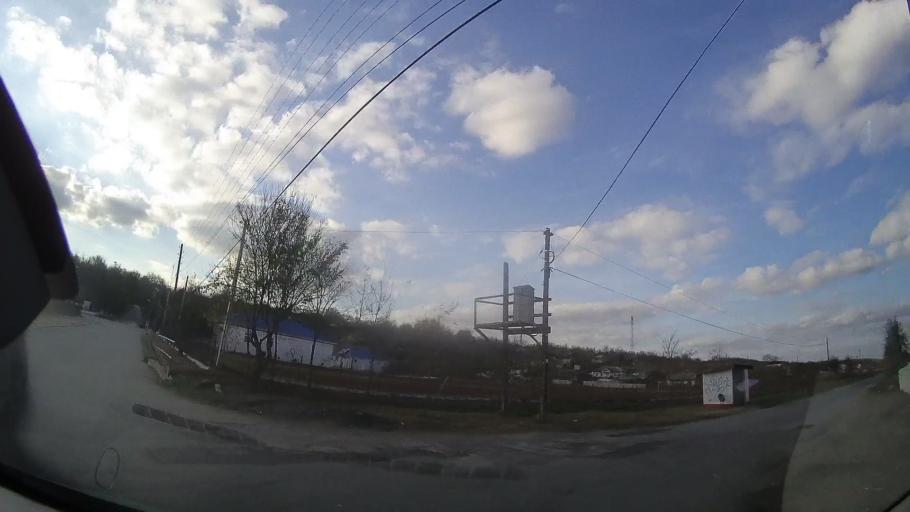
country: RO
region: Constanta
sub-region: Comuna Cerchezu
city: Cerchezu
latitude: 43.8244
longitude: 28.0978
